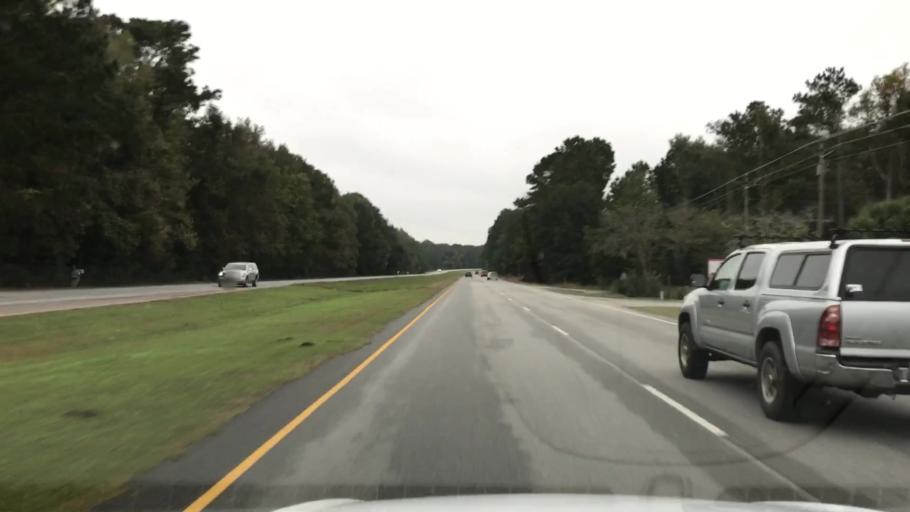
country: US
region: South Carolina
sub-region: Charleston County
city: Awendaw
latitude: 32.9301
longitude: -79.7135
